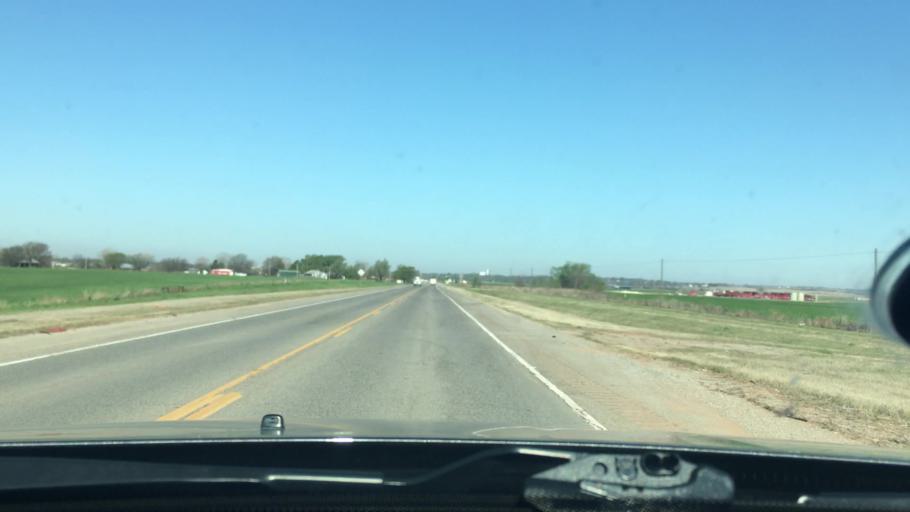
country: US
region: Oklahoma
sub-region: Garvin County
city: Lindsay
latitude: 34.8314
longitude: -97.5749
